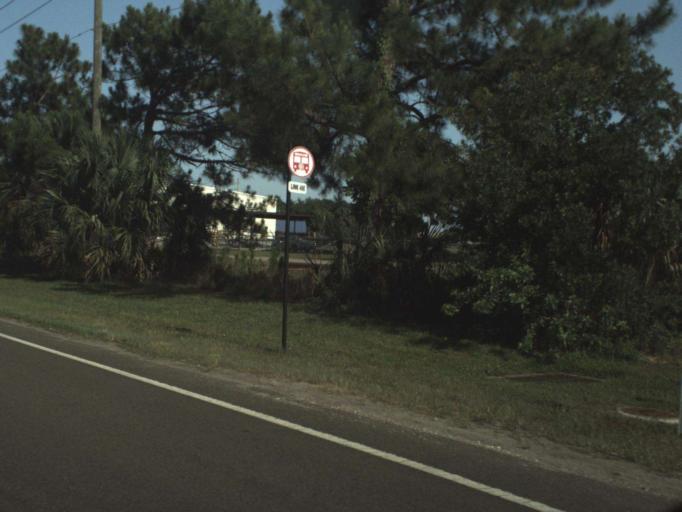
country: US
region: Florida
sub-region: Seminole County
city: Midway
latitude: 28.7868
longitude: -81.2223
